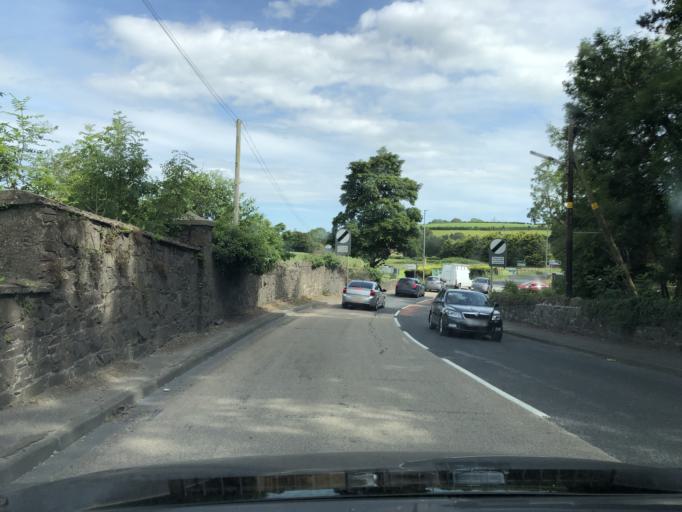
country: GB
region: Northern Ireland
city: Ballynahinch
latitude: 54.3947
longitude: -5.8865
